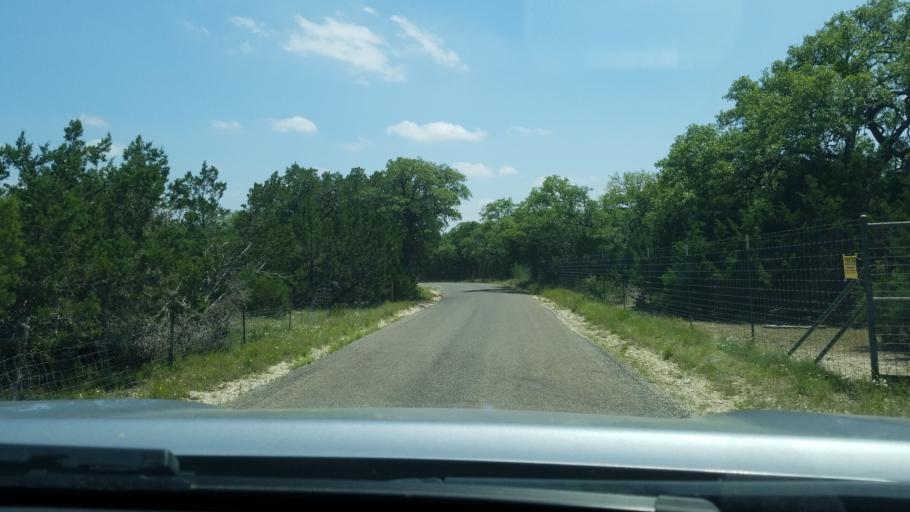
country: US
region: Texas
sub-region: Blanco County
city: Blanco
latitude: 30.0786
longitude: -98.4005
